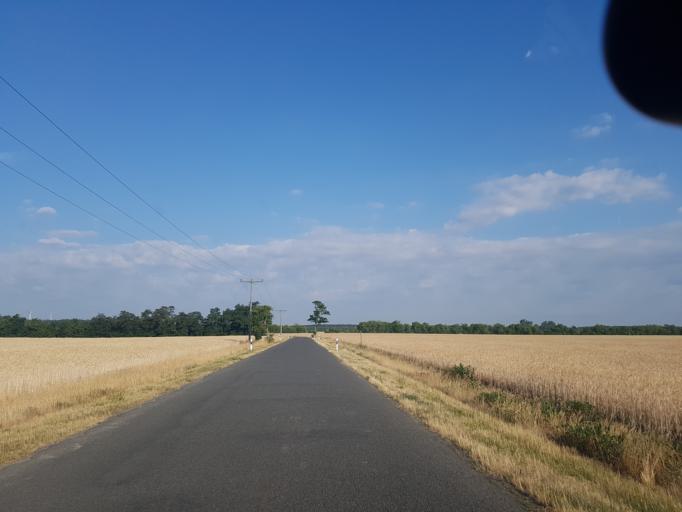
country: DE
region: Saxony-Anhalt
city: Seyda
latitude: 51.9225
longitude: 12.9331
